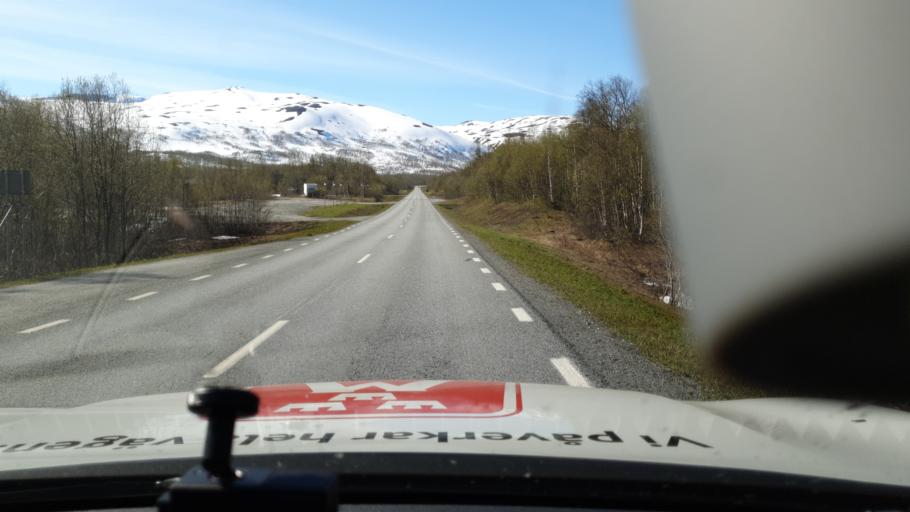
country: NO
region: Nordland
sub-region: Rana
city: Mo i Rana
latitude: 65.8748
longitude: 15.0067
